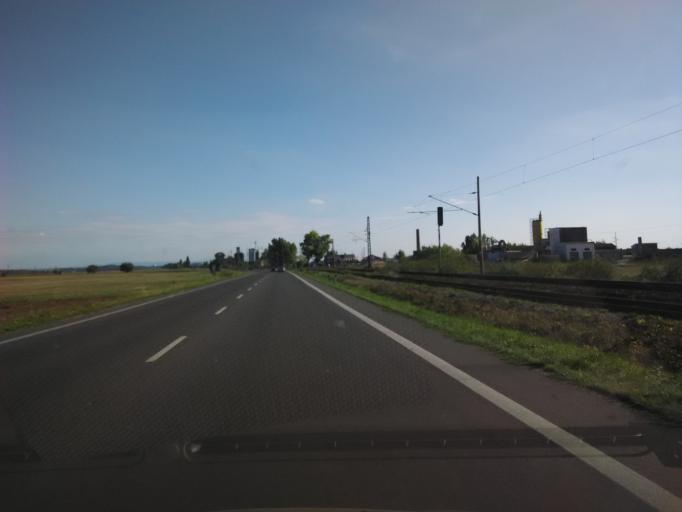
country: SK
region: Nitriansky
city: Tlmace
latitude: 48.2865
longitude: 18.5438
